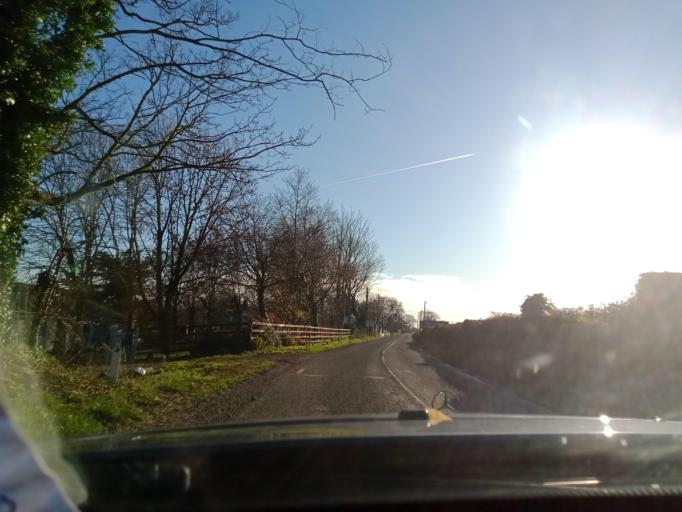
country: IE
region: Leinster
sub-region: Kilkenny
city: Piltown
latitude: 52.3727
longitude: -7.3373
